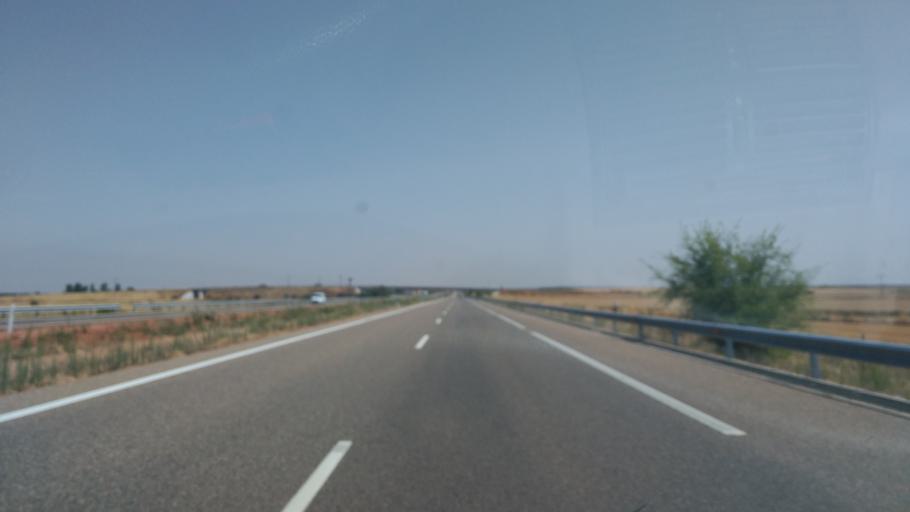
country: ES
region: Castille and Leon
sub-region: Provincia de Salamanca
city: Calzada de Don Diego
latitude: 40.8980
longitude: -5.9150
